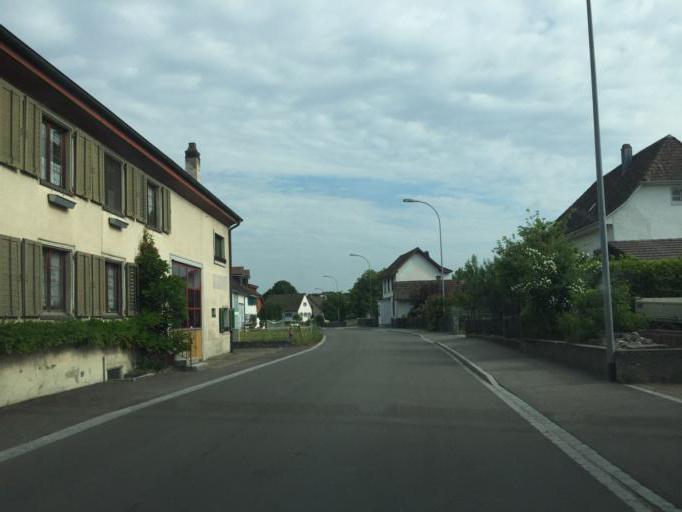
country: CH
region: Zurich
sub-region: Bezirk Andelfingen
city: Dachsen
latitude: 47.6393
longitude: 8.6000
